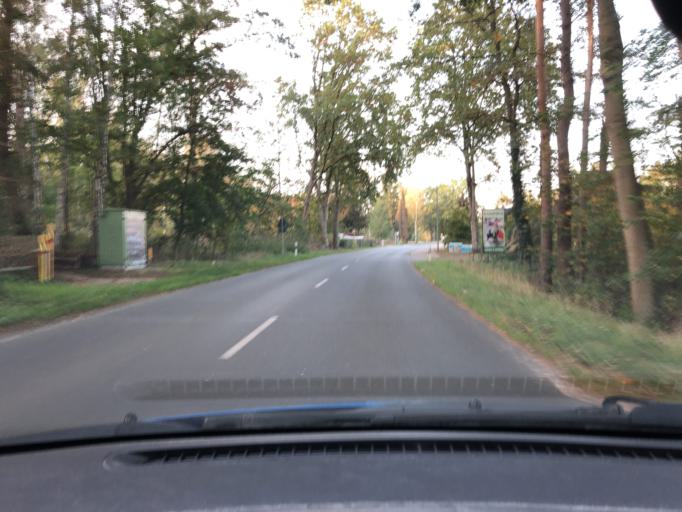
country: DE
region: Lower Saxony
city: Hitzacker
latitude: 53.1359
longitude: 11.0459
